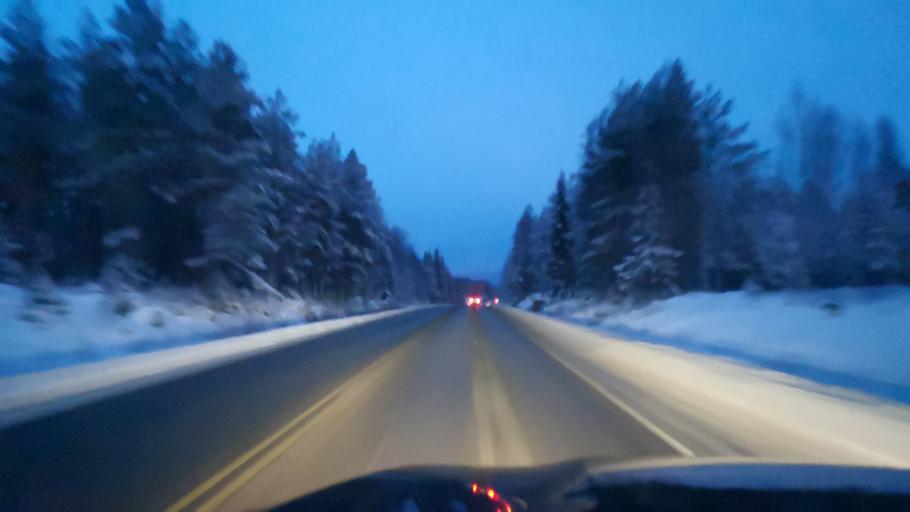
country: FI
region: Varsinais-Suomi
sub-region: Loimaa
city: Loimaa
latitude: 60.8709
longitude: 23.0612
